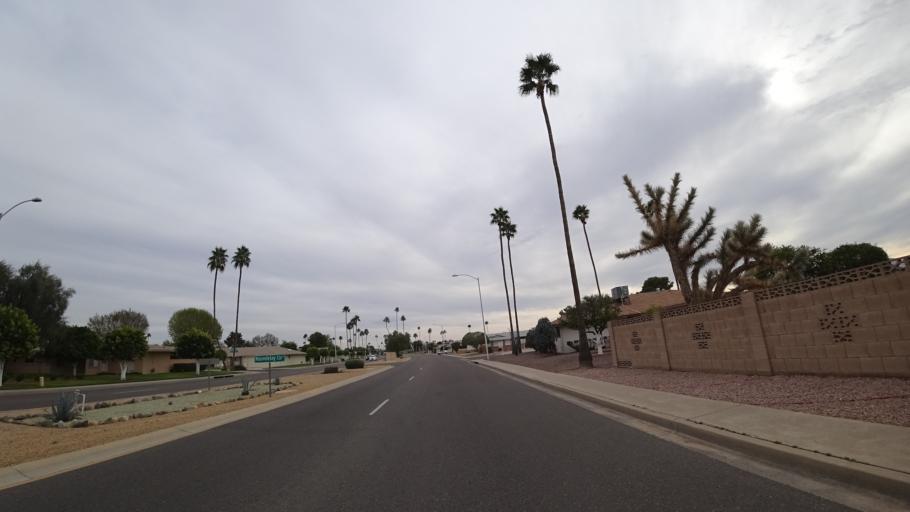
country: US
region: Arizona
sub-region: Maricopa County
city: Youngtown
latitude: 33.6153
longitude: -112.2912
